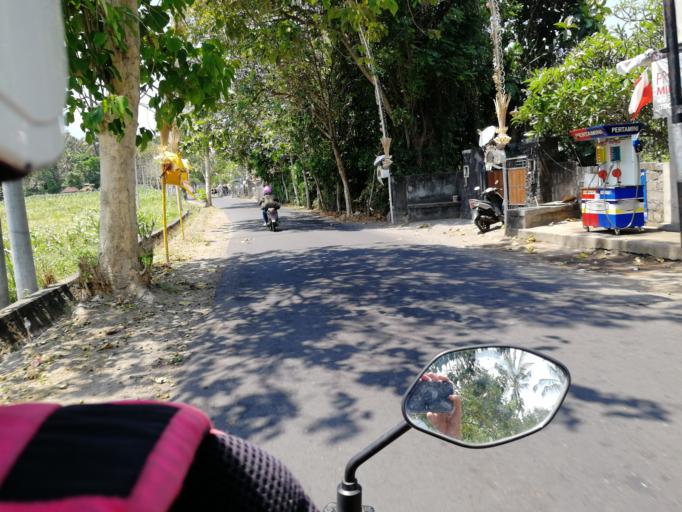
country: ID
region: Bali
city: Banjar Timbrah
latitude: -8.4687
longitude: 115.5919
